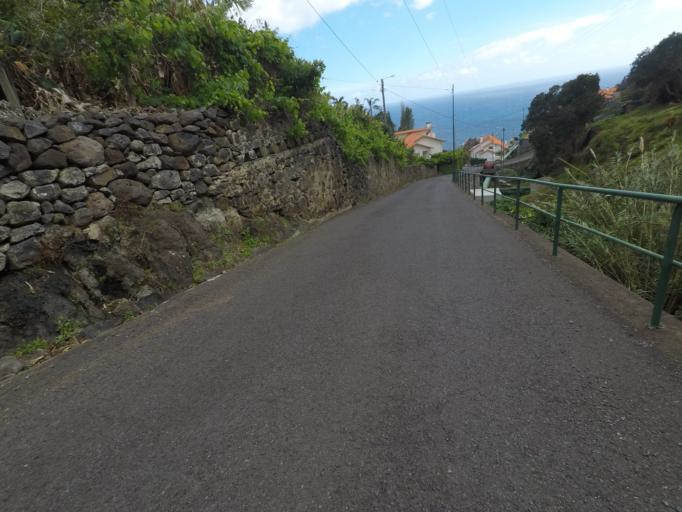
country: PT
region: Madeira
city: Calheta
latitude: 32.7264
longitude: -17.1774
